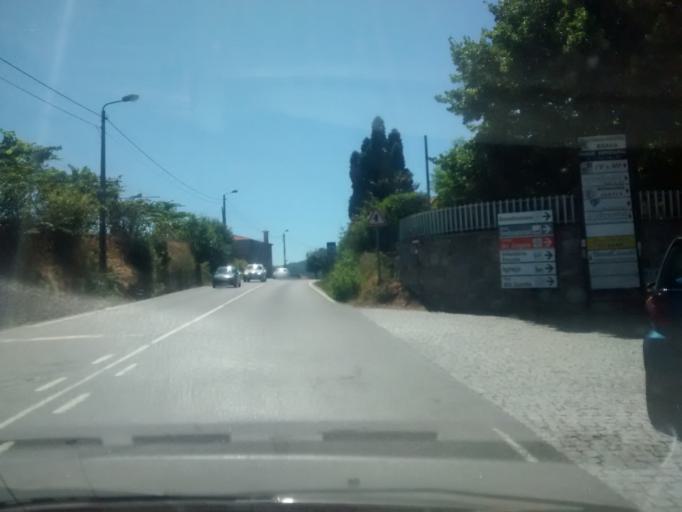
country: PT
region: Braga
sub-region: Braga
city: Braga
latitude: 41.5345
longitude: -8.4571
